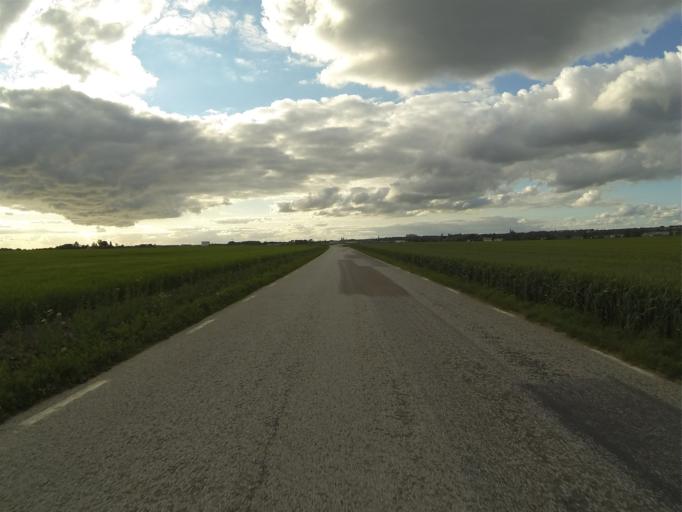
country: SE
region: Skane
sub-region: Staffanstorps Kommun
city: Staffanstorp
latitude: 55.6757
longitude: 13.2304
